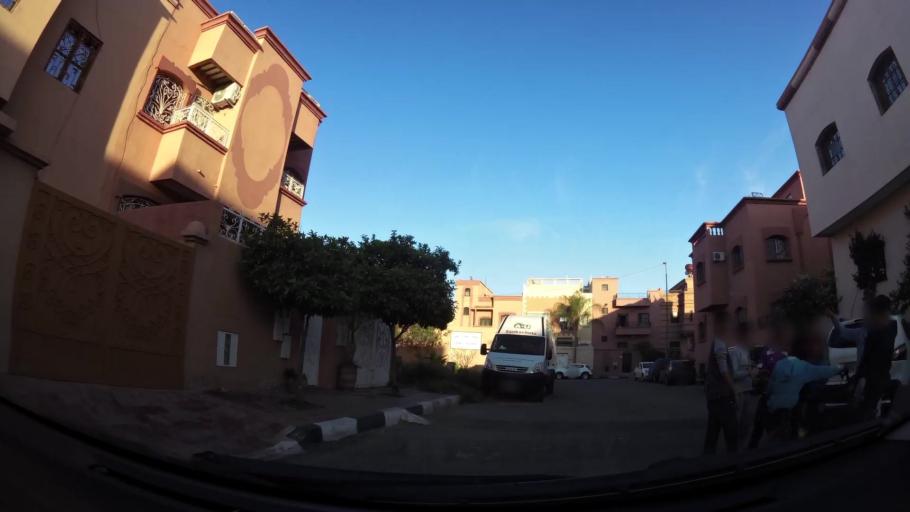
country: MA
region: Marrakech-Tensift-Al Haouz
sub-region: Marrakech
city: Marrakesh
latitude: 31.6240
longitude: -8.0324
